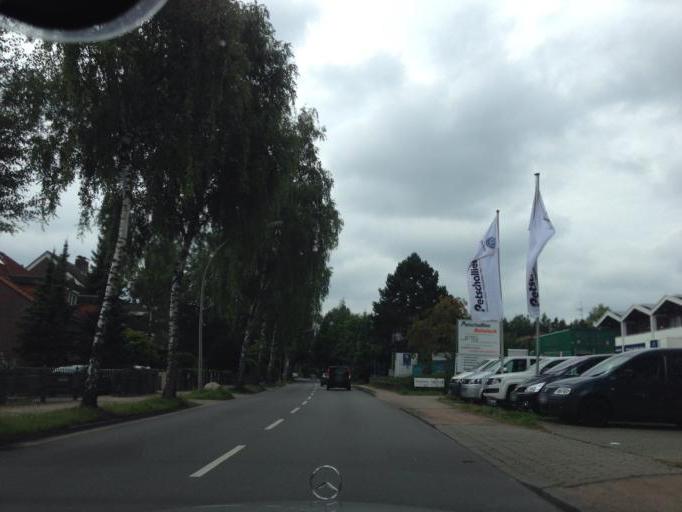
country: DE
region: Hamburg
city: Sasel
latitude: 53.6431
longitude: 10.1258
